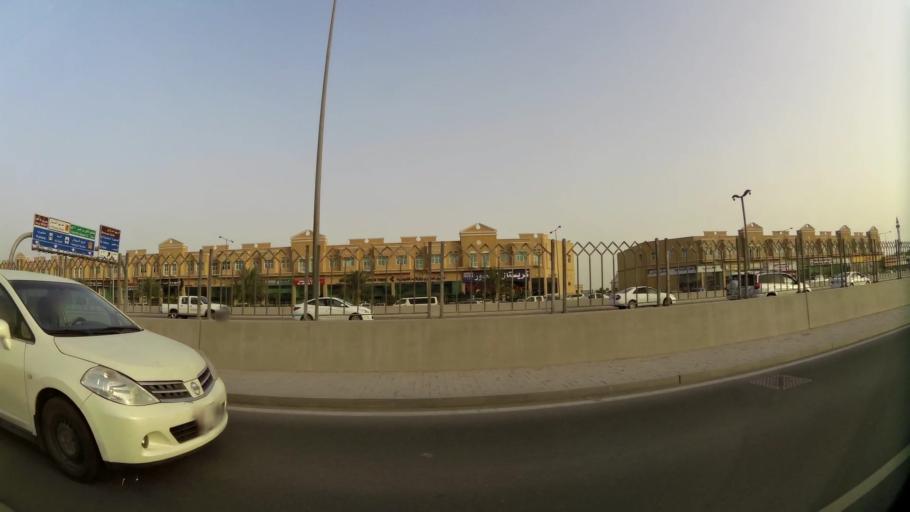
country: QA
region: Baladiyat ar Rayyan
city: Ar Rayyan
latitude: 25.2390
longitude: 51.4541
